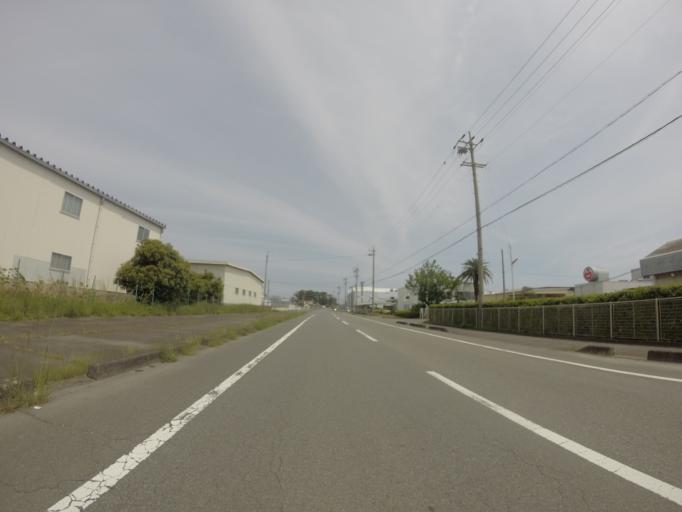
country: JP
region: Shizuoka
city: Yaizu
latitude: 34.7833
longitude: 138.2990
